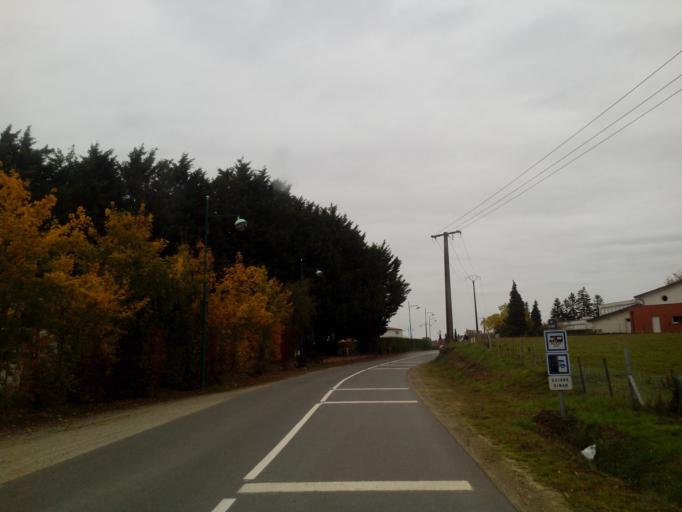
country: FR
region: Brittany
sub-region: Departement du Morbihan
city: Mauron
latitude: 48.0759
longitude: -2.2926
